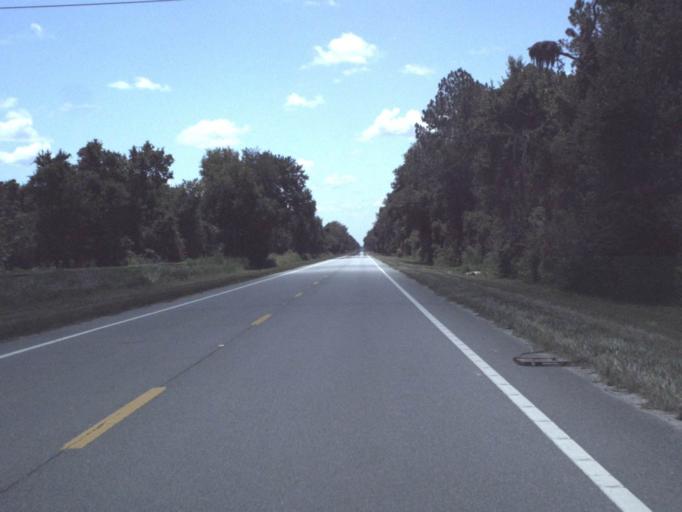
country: US
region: Florida
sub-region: Hamilton County
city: Jasper
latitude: 30.4316
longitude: -82.8673
